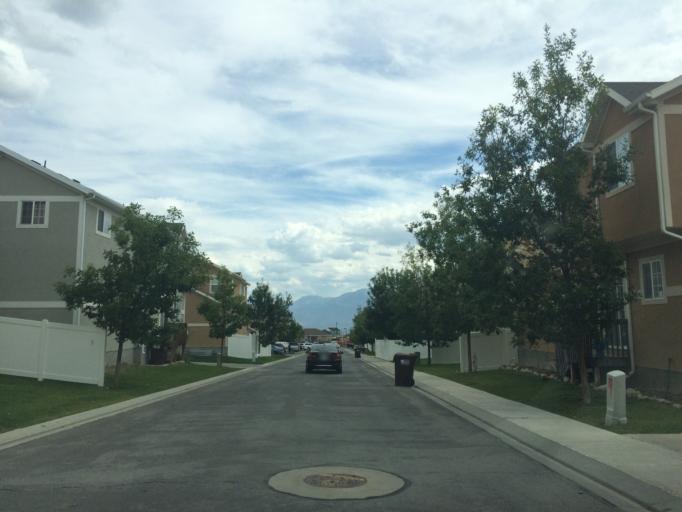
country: US
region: Utah
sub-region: Salt Lake County
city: Oquirrh
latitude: 40.6118
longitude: -112.0541
